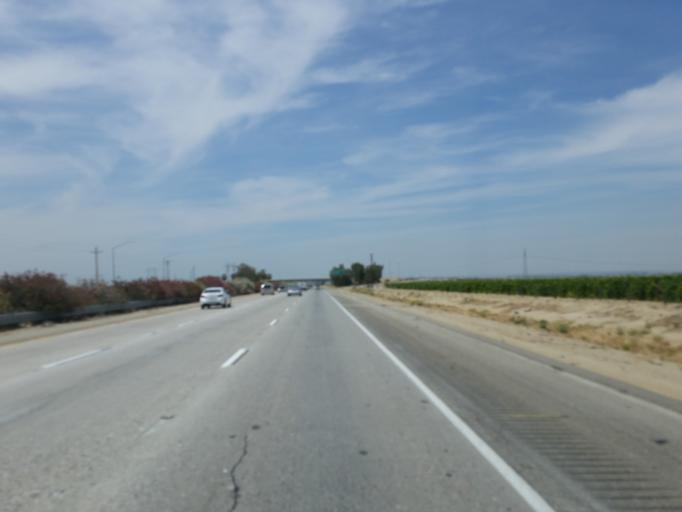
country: US
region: California
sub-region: Kern County
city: Weedpatch
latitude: 35.1164
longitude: -118.9863
